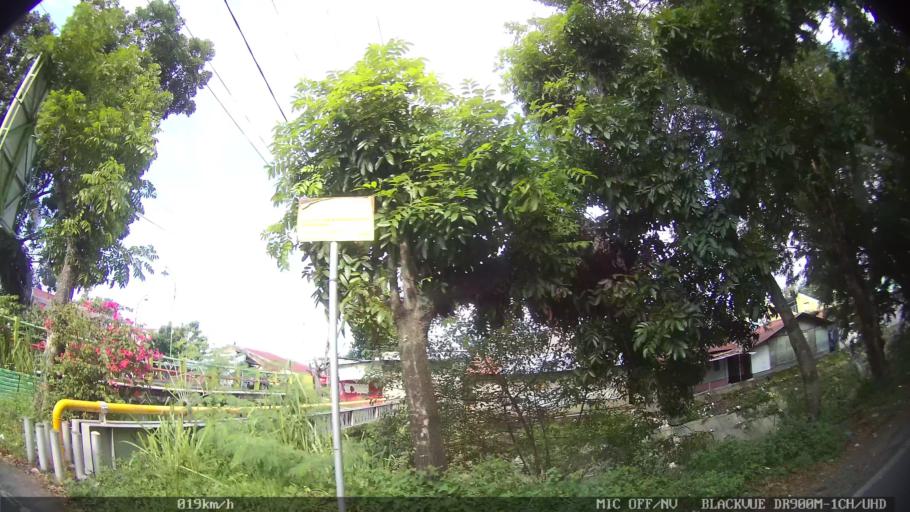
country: ID
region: North Sumatra
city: Medan
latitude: 3.6162
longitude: 98.6634
